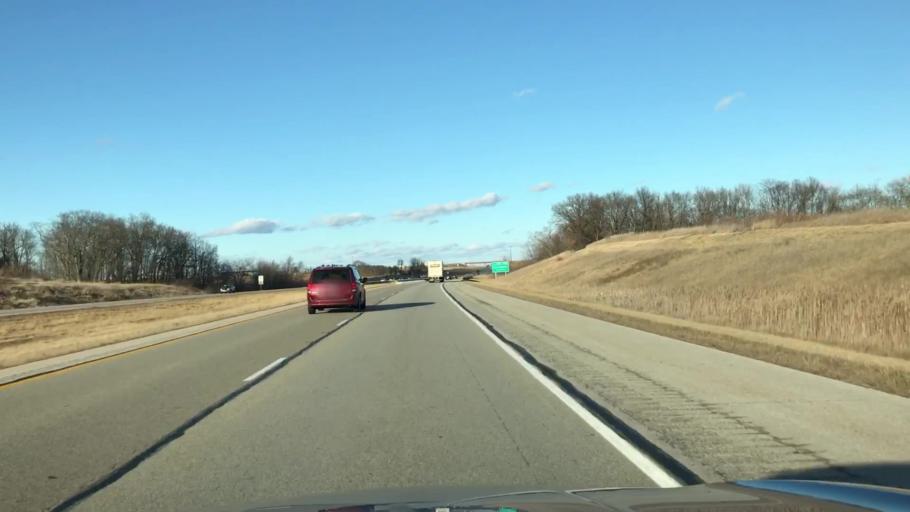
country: US
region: Illinois
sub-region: McLean County
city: Lexington
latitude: 40.6329
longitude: -88.8150
